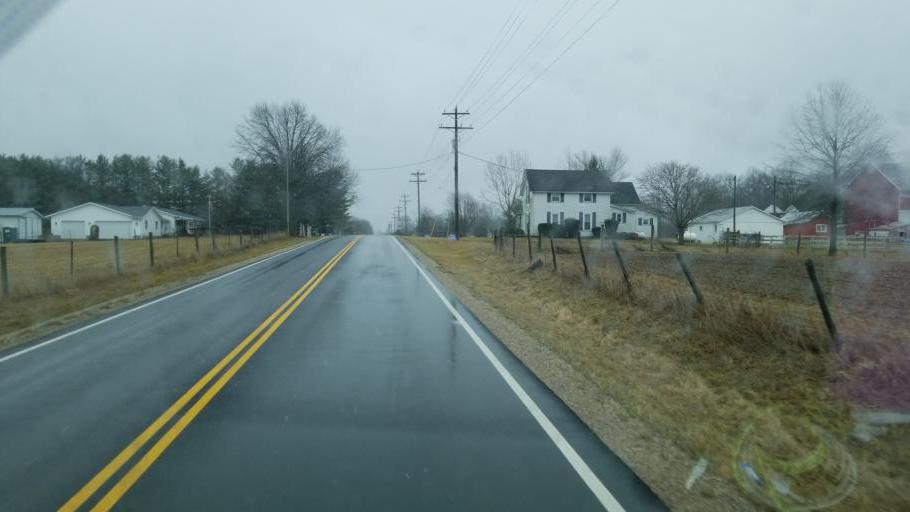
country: US
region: Ohio
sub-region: Union County
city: New California
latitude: 40.2144
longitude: -83.2757
